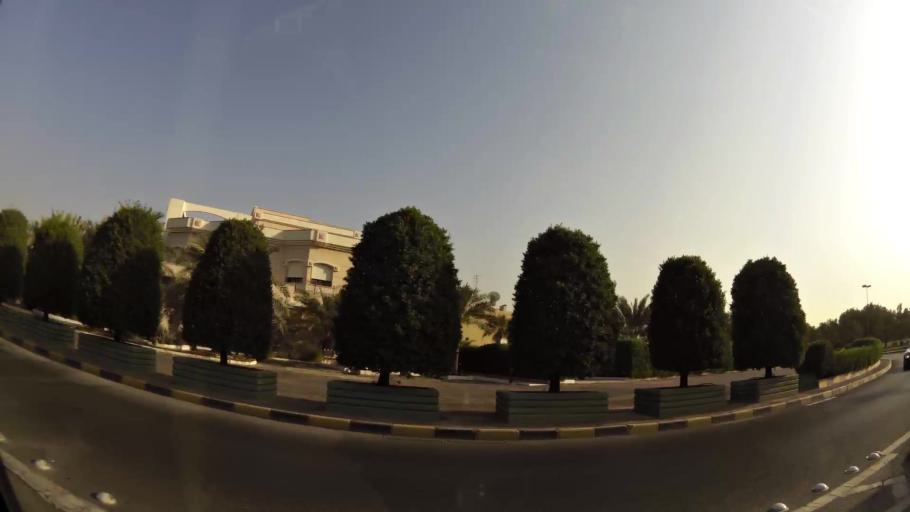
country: KW
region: Al Asimah
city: Ad Dasmah
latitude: 29.3503
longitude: 48.0126
